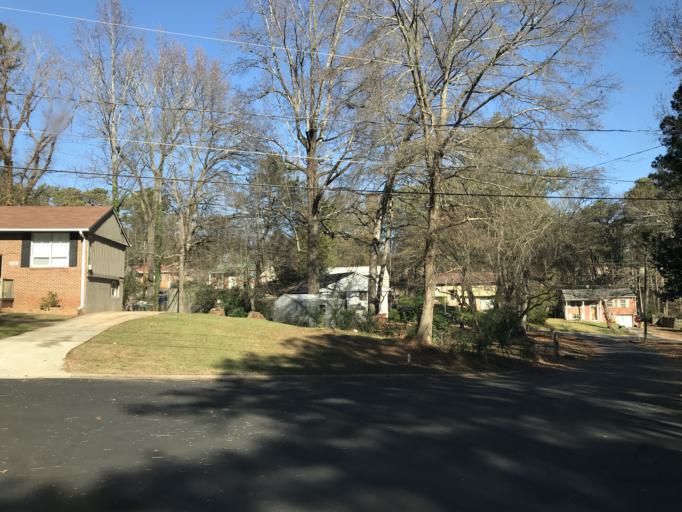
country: US
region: Georgia
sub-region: Clayton County
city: Morrow
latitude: 33.5787
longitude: -84.3585
